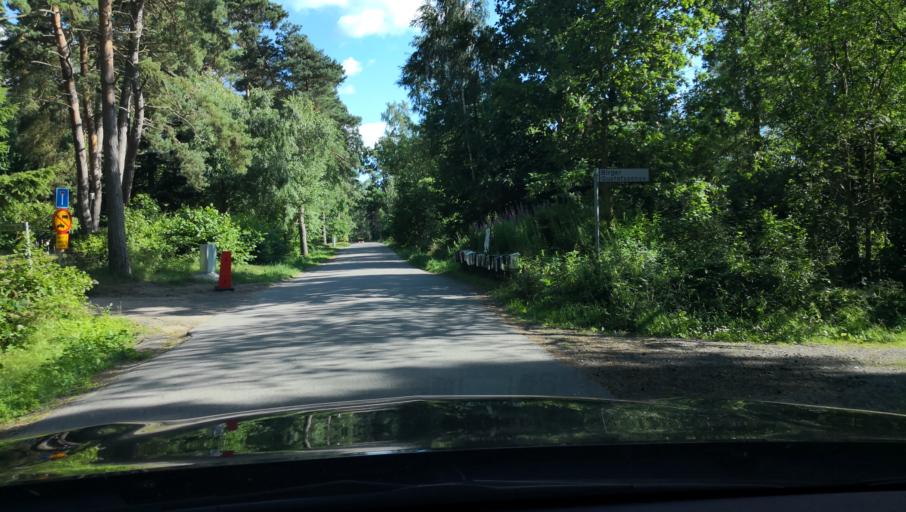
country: SE
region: Skane
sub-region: Simrishamns Kommun
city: Kivik
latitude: 55.7797
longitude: 14.1941
